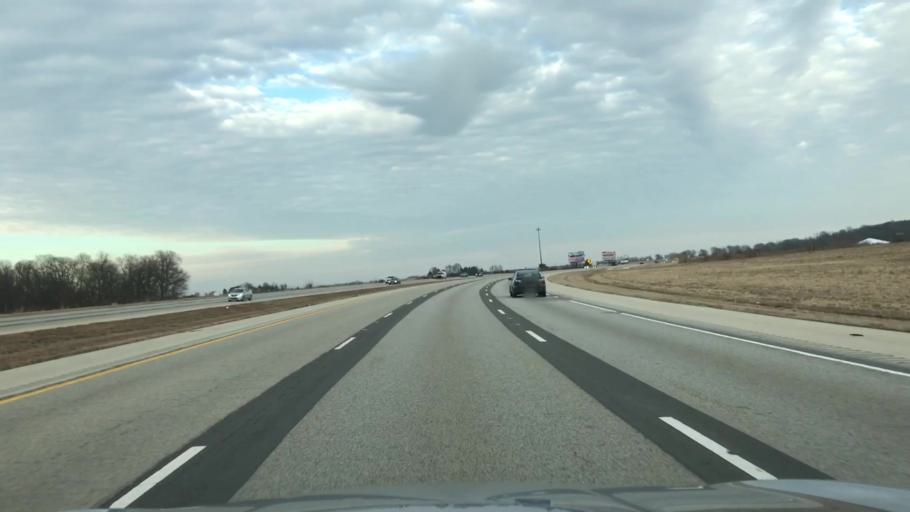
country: US
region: Illinois
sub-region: Sangamon County
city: Williamsville
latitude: 40.0215
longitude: -89.4949
